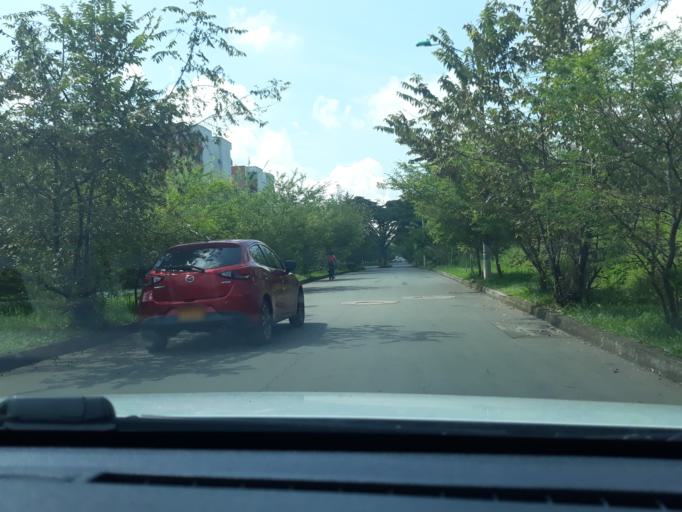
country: CO
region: Valle del Cauca
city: Cali
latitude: 3.3579
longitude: -76.5205
